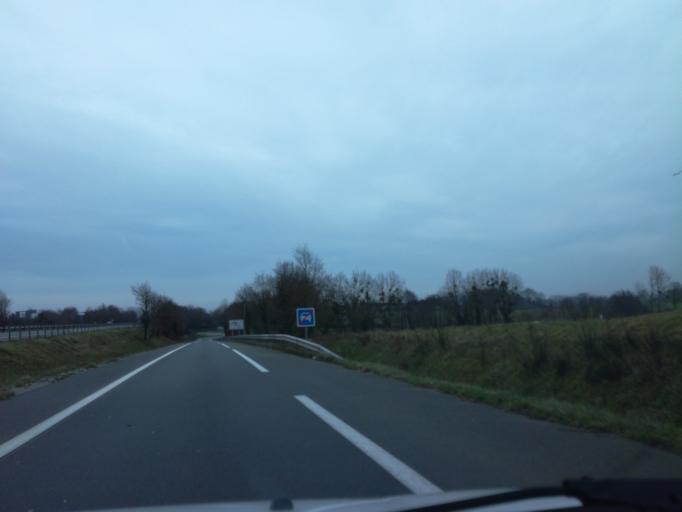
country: FR
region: Brittany
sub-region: Departement d'Ille-et-Vilaine
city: Torce
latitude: 48.0753
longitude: -1.2742
